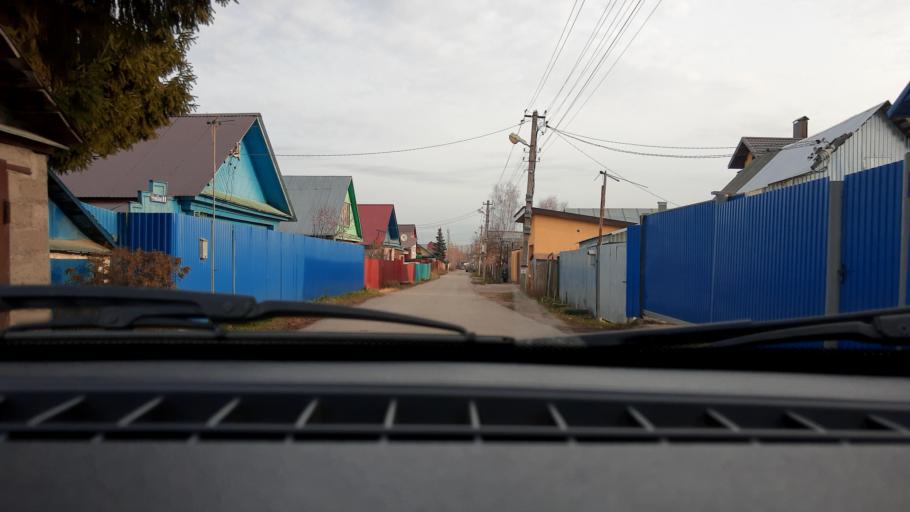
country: RU
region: Bashkortostan
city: Mikhaylovka
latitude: 54.7819
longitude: 55.8951
